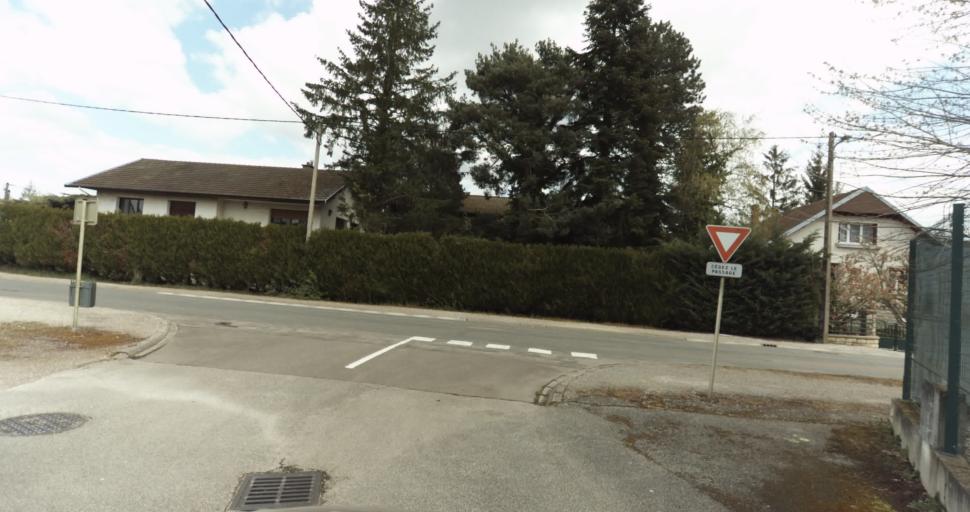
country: FR
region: Bourgogne
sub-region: Departement de la Cote-d'Or
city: Auxonne
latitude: 47.1881
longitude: 5.3902
